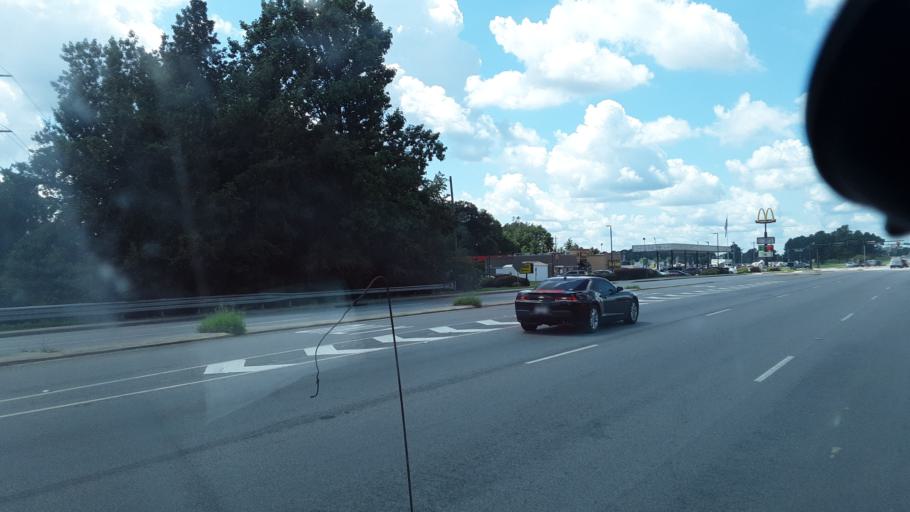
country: US
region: South Carolina
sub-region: Berkeley County
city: Sangaree
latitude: 33.0399
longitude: -80.1408
